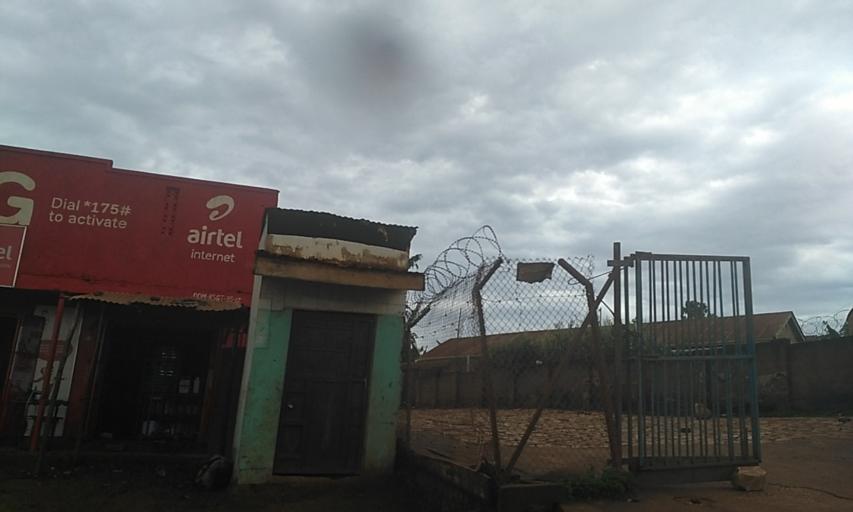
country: UG
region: Central Region
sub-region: Wakiso District
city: Kireka
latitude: 0.4372
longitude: 32.6033
